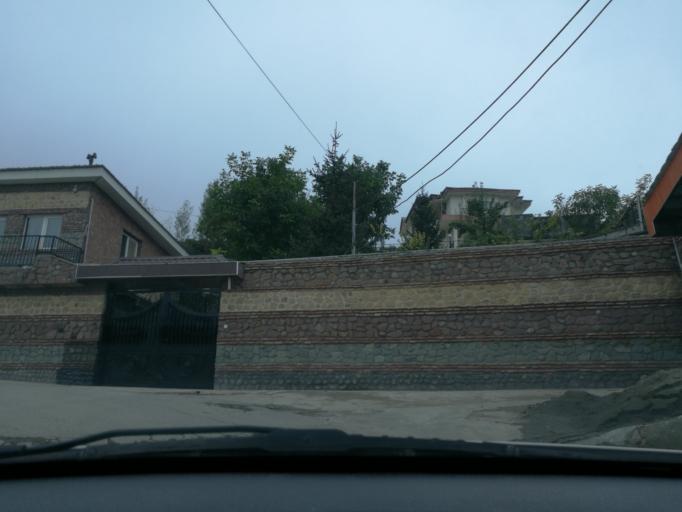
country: IR
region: Mazandaran
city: `Abbasabad
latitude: 36.4976
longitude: 51.2076
